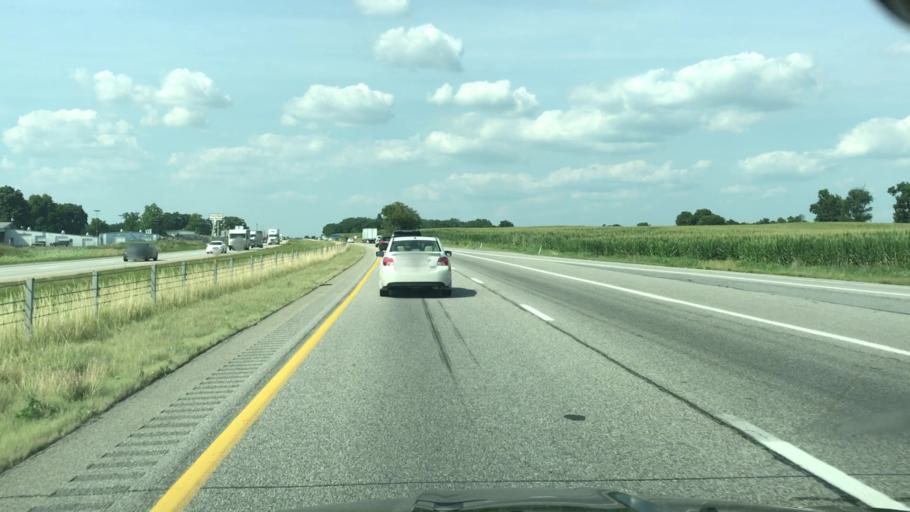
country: US
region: Pennsylvania
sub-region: Franklin County
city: State Line
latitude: 39.7575
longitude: -77.7259
